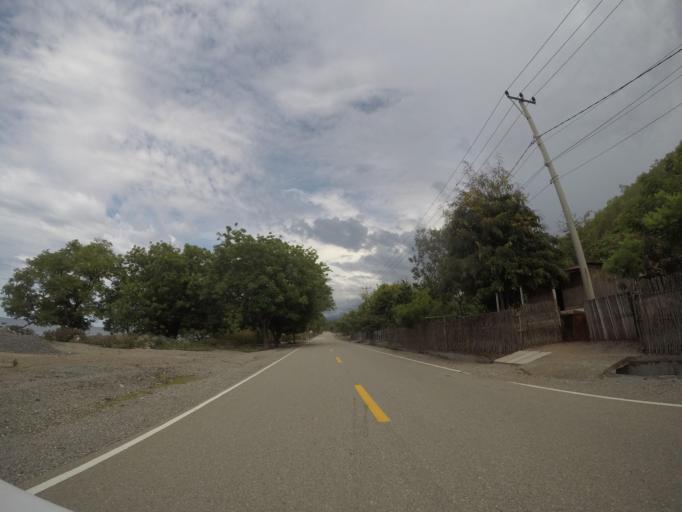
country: TL
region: Liquica
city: Maubara
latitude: -8.6115
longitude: 125.1983
